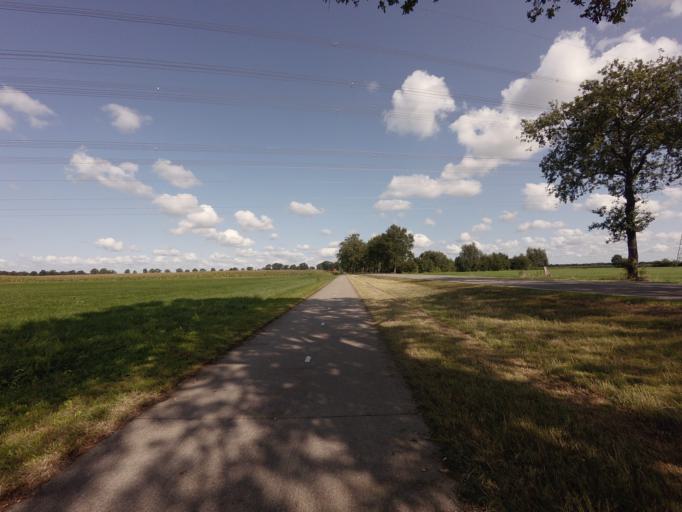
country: NL
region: Overijssel
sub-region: Gemeente Dalfsen
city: Dalfsen
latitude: 52.5428
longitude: 6.2616
